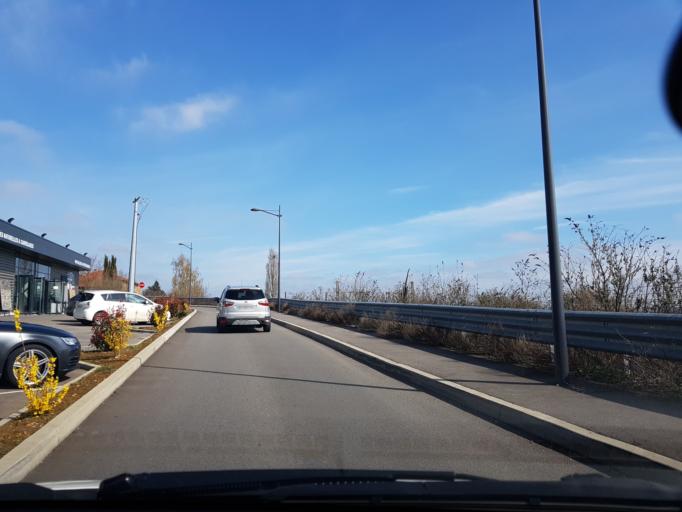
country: FR
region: Rhone-Alpes
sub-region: Departement du Rhone
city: Pommiers
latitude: 45.9594
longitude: 4.7158
